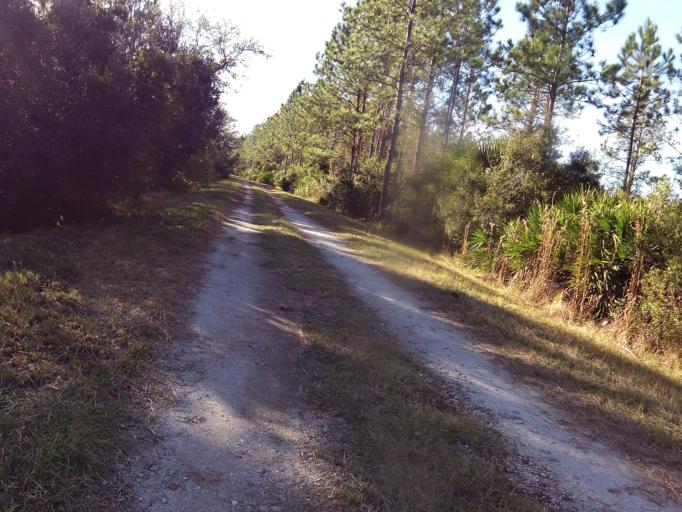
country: US
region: Florida
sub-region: Putnam County
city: Palatka
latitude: 29.6828
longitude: -81.7345
